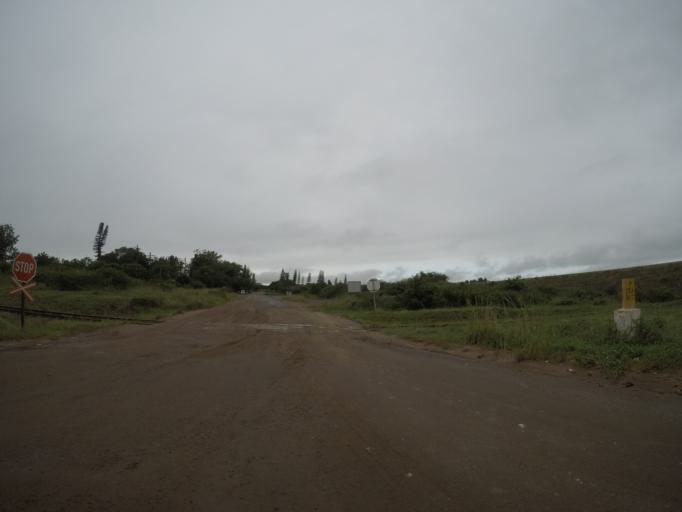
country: ZA
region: KwaZulu-Natal
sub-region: uThungulu District Municipality
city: Empangeni
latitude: -28.6618
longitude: 31.7844
